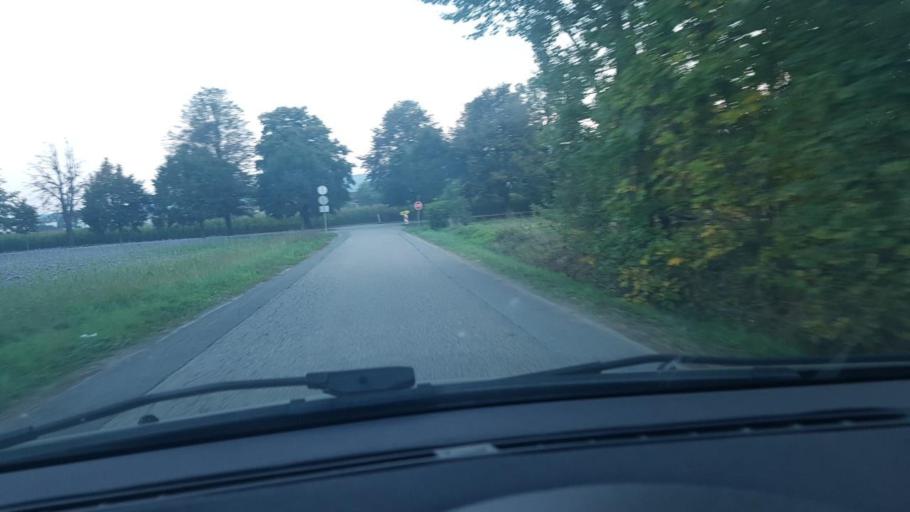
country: SI
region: Maribor
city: Razvanje
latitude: 46.5032
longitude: 15.6372
